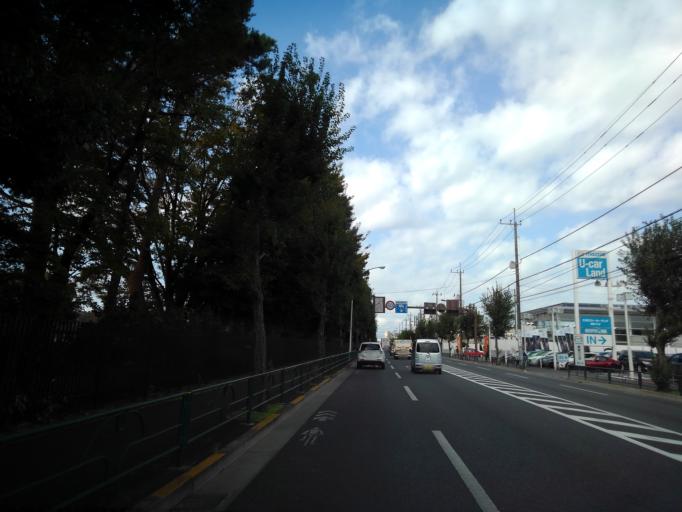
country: JP
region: Tokyo
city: Higashimurayama-shi
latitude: 35.7466
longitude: 139.4853
